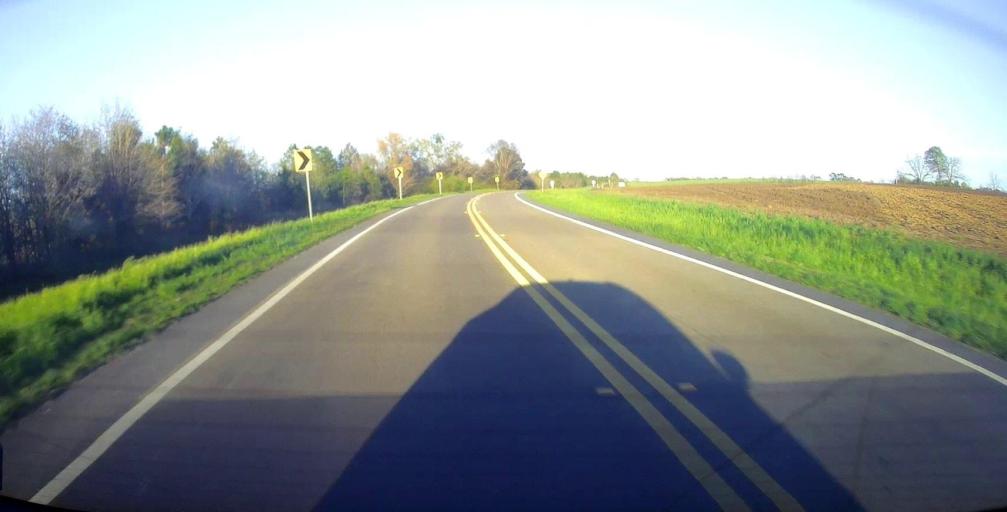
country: US
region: Georgia
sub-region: Wilcox County
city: Rochelle
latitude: 31.9484
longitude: -83.5071
